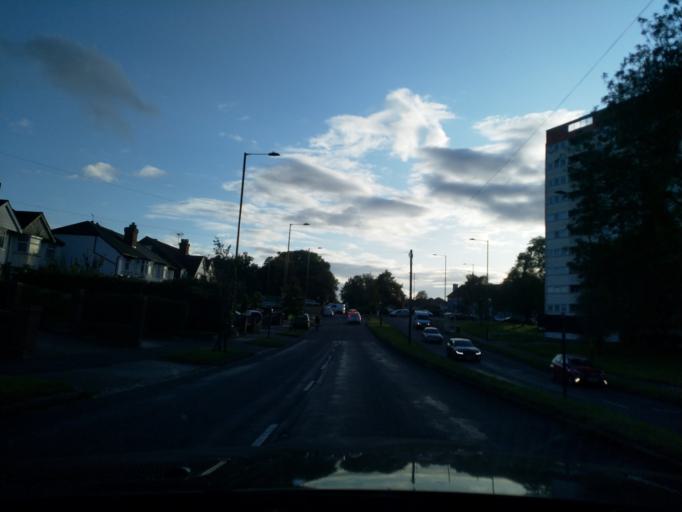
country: GB
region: England
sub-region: Worcestershire
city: Alvechurch
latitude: 52.3950
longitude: -1.9522
